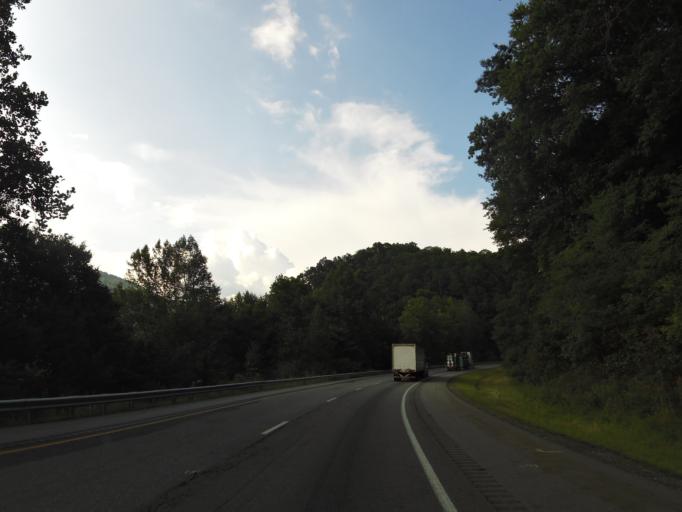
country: US
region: North Carolina
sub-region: Haywood County
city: Cove Creek
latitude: 35.7193
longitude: -83.0378
